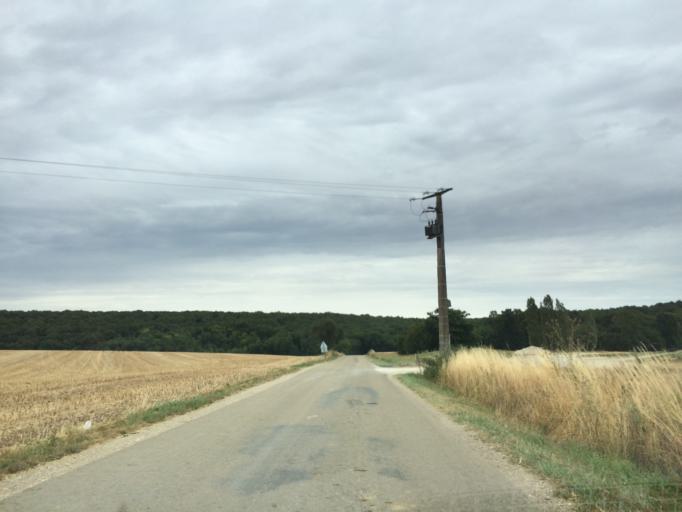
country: FR
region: Bourgogne
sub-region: Departement de l'Yonne
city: Aillant-sur-Tholon
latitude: 47.8569
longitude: 3.2739
